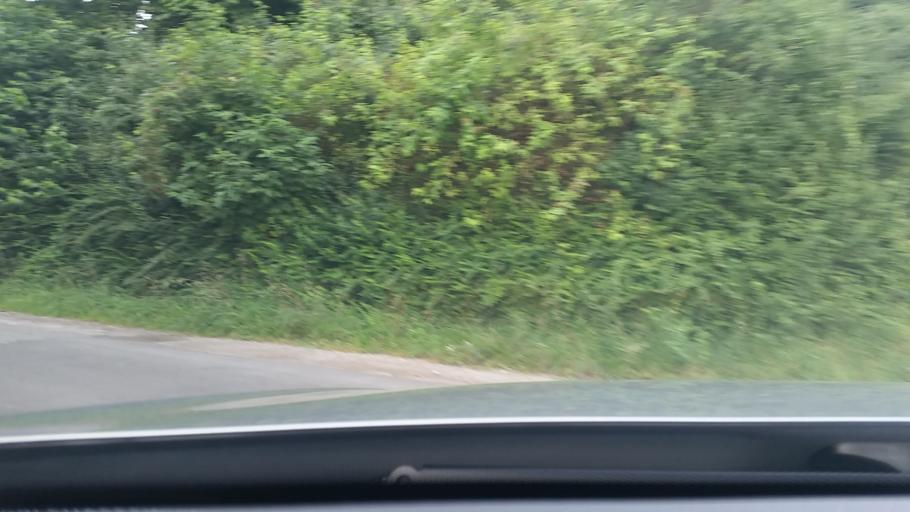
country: DE
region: Lower Saxony
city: Langenhagen
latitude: 52.4085
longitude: 9.7676
